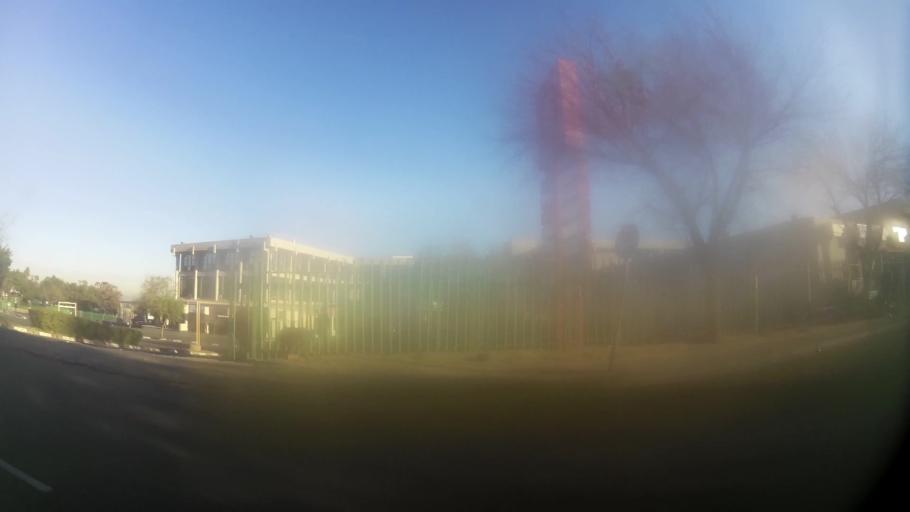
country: ZA
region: Gauteng
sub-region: City of Johannesburg Metropolitan Municipality
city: Midrand
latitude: -25.9983
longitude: 28.1268
